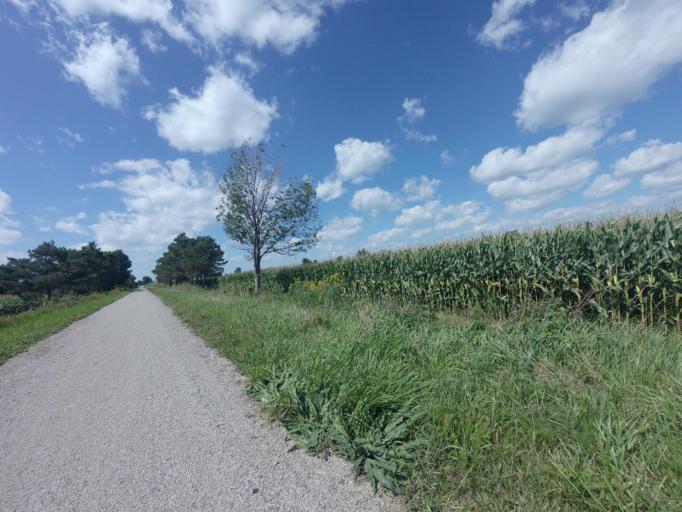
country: CA
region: Ontario
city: Huron East
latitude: 43.6617
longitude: -81.2545
